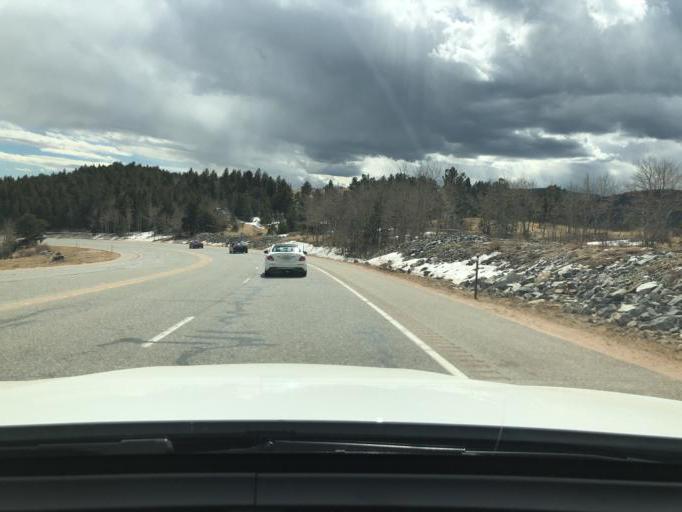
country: US
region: Colorado
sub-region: Gilpin County
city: Central City
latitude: 39.7862
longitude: -105.4958
